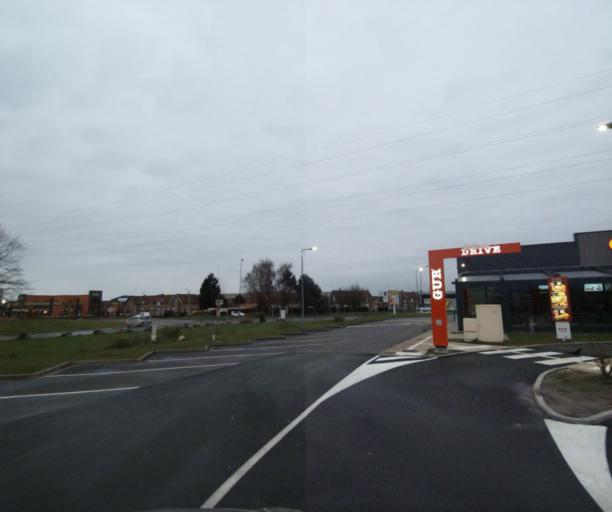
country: FR
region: Nord-Pas-de-Calais
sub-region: Departement du Nord
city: Raismes
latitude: 50.3812
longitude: 3.4779
